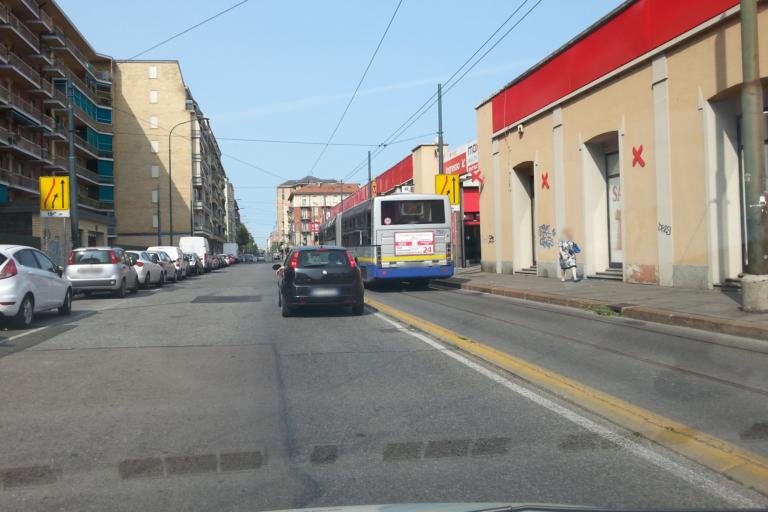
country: IT
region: Piedmont
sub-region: Provincia di Torino
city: Moncalieri
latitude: 45.0218
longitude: 7.6652
